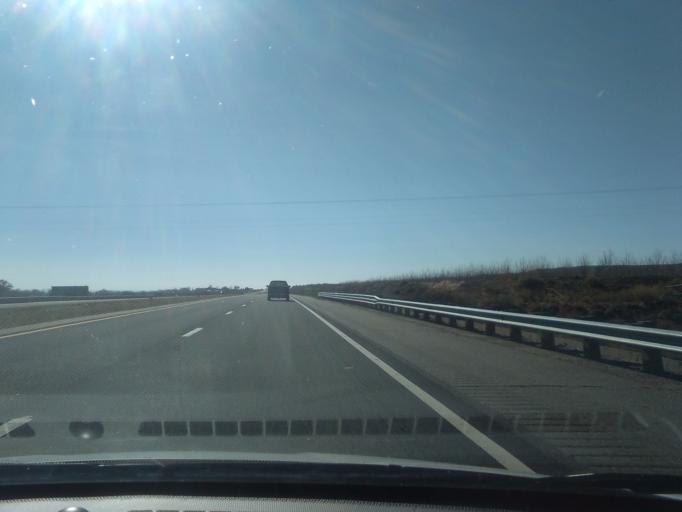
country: US
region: New Mexico
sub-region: Valencia County
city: Jarales
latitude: 34.6115
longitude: -106.7859
